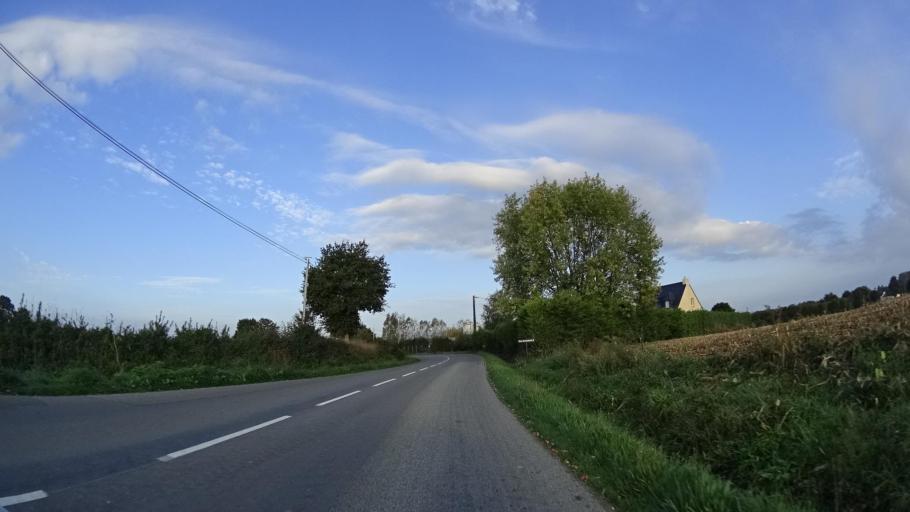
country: FR
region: Brittany
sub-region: Departement des Cotes-d'Armor
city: Plouasne
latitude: 48.2811
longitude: -2.0052
